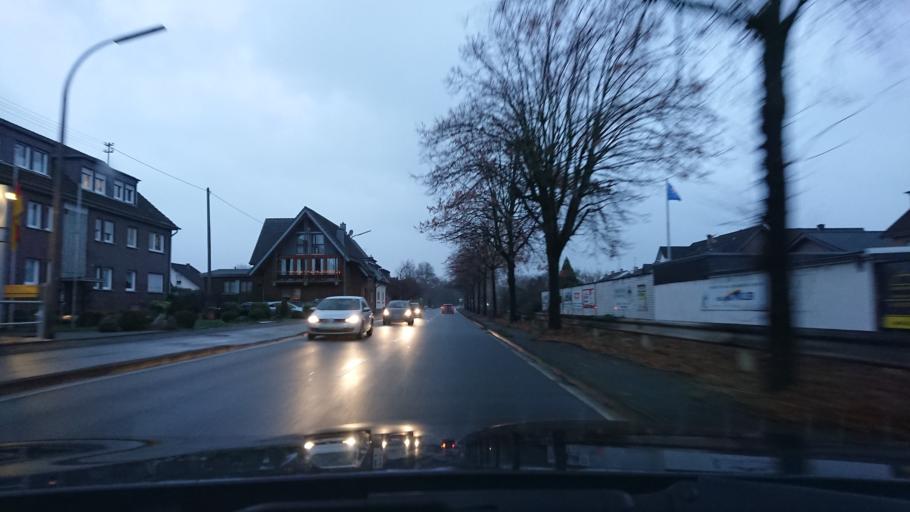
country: DE
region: North Rhine-Westphalia
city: Niederkassel
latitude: 50.7803
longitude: 7.0669
